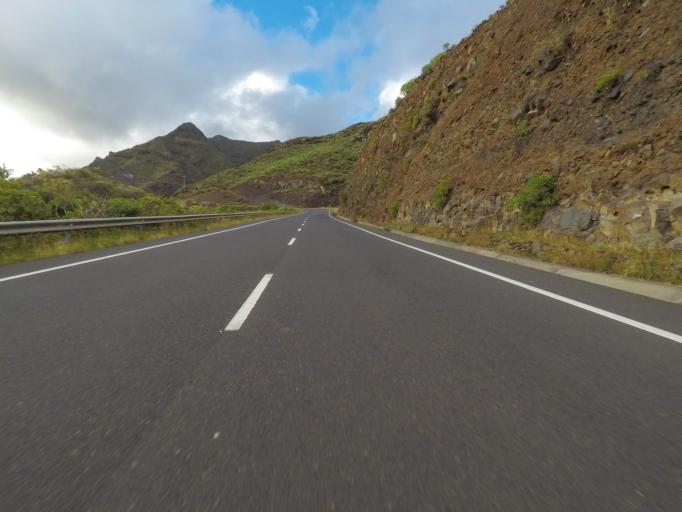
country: ES
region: Canary Islands
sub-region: Provincia de Santa Cruz de Tenerife
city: San Sebastian de la Gomera
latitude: 28.1185
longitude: -17.1424
